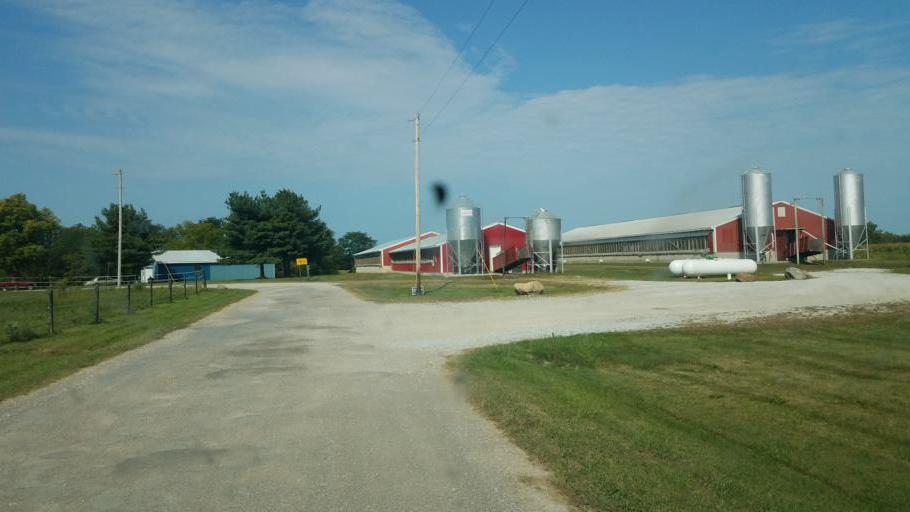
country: US
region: Ohio
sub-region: Morrow County
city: Cardington
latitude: 40.4845
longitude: -82.9546
